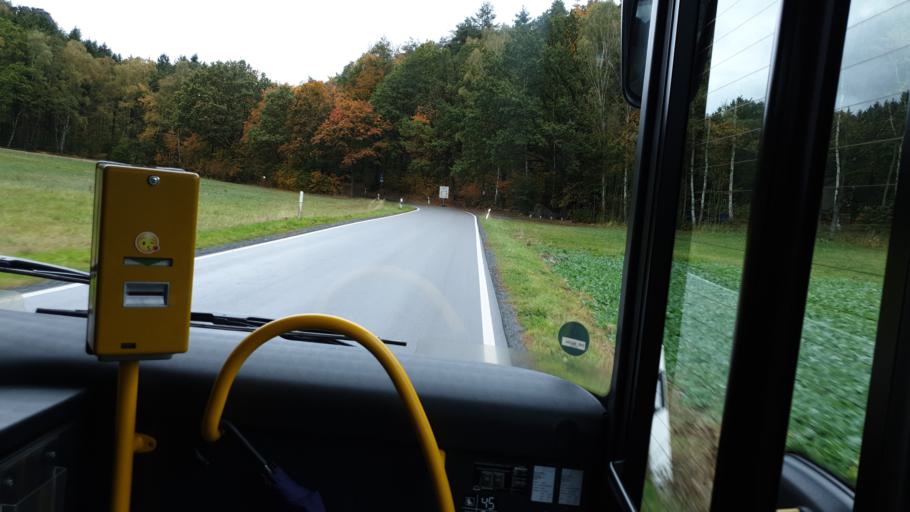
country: DE
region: Saxony
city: Kurort Gohrisch
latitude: 50.8990
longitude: 14.1187
